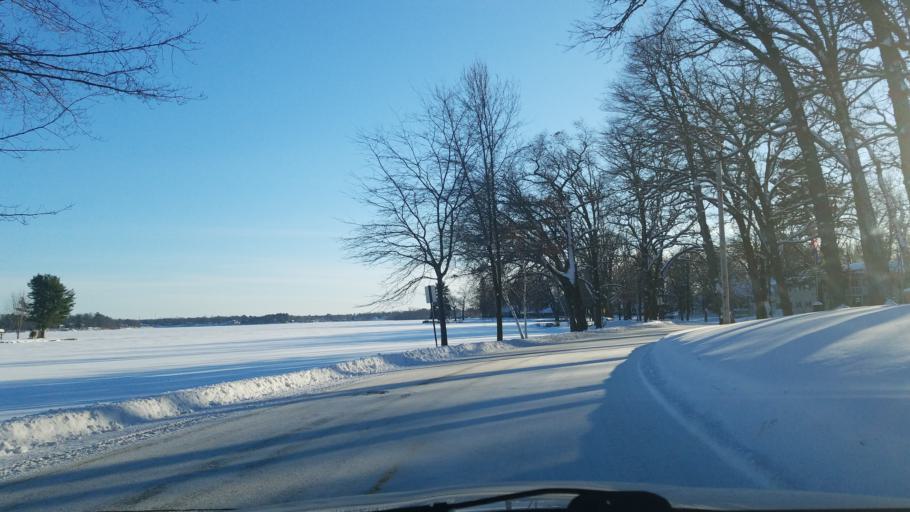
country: US
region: Wisconsin
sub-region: Barron County
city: Rice Lake
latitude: 45.5080
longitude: -91.7310
